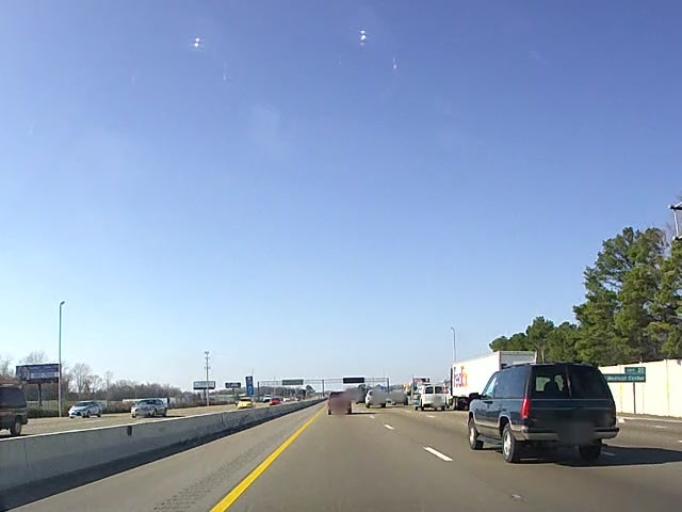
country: US
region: Tennessee
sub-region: Shelby County
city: Germantown
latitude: 35.0785
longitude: -89.9206
